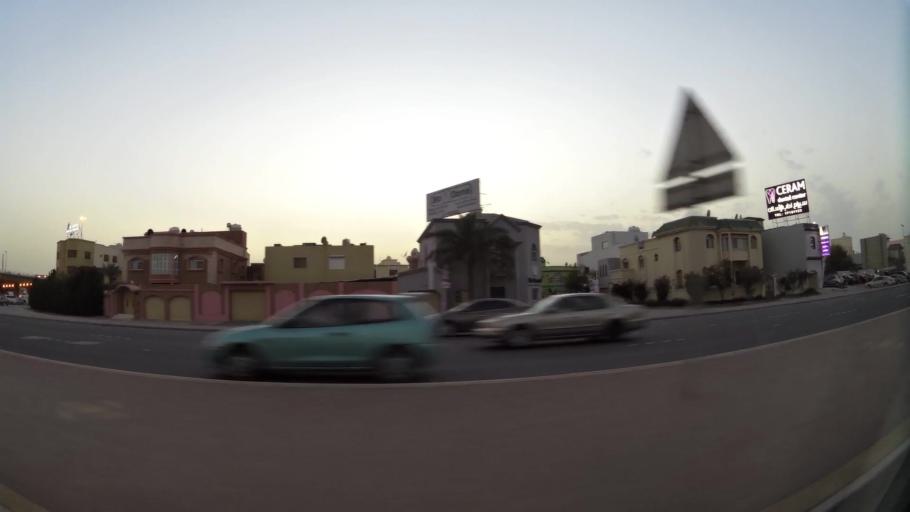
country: BH
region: Manama
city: Manama
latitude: 26.2064
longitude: 50.5674
